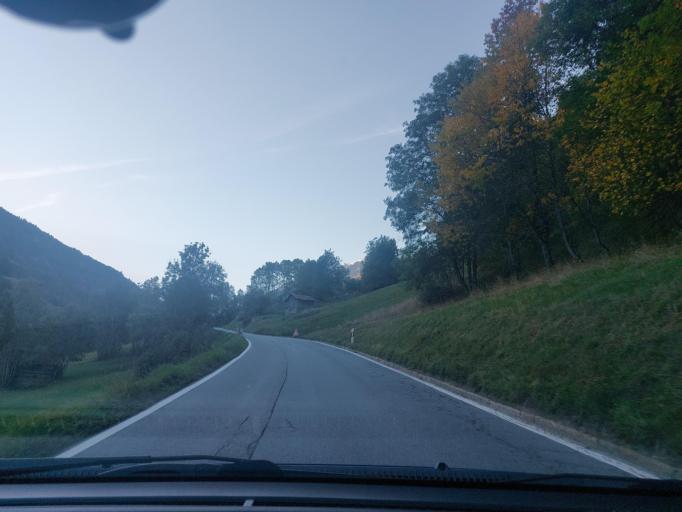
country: CH
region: Valais
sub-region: Sierre District
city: Chippis
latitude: 46.2069
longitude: 7.5830
